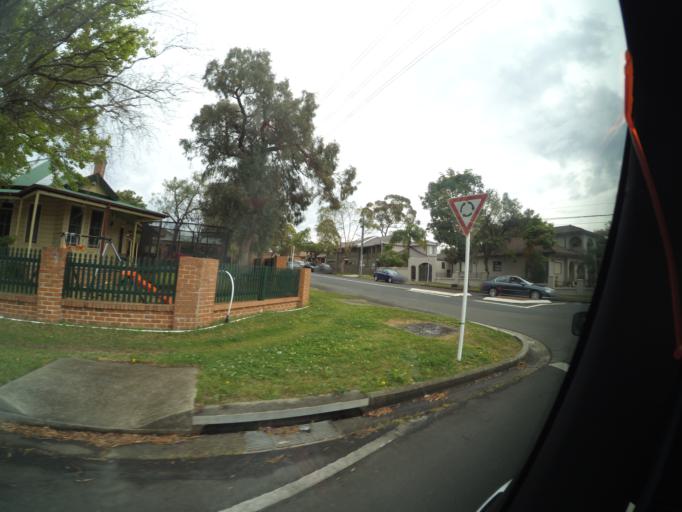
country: AU
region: New South Wales
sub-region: Bankstown
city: Bankstown
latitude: -33.9234
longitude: 151.0252
